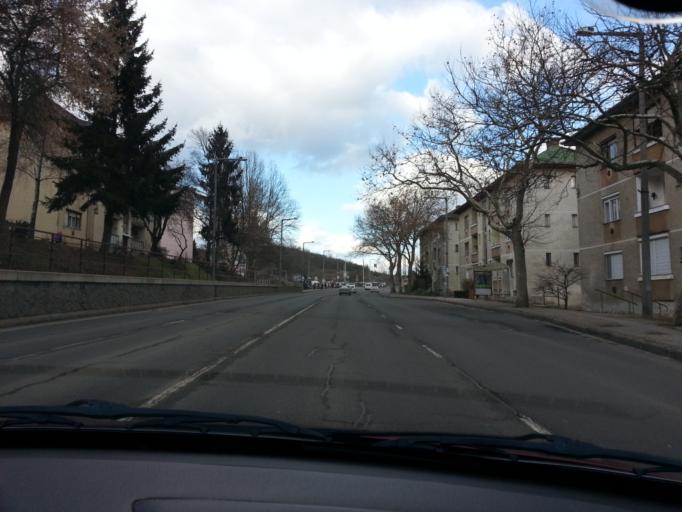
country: HU
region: Nograd
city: Salgotarjan
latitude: 48.0732
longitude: 19.7843
